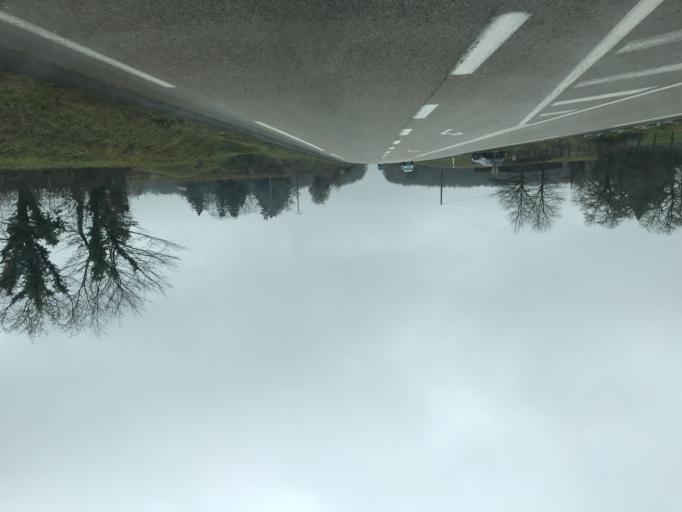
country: FR
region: Rhone-Alpes
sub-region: Departement de l'Ain
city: Peronnas
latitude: 46.1786
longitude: 5.1944
